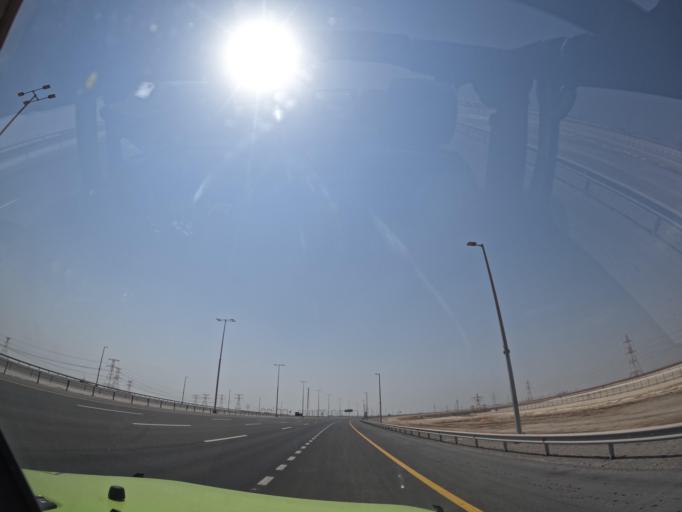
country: AE
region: Abu Dhabi
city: Abu Dhabi
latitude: 24.1613
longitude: 54.3518
